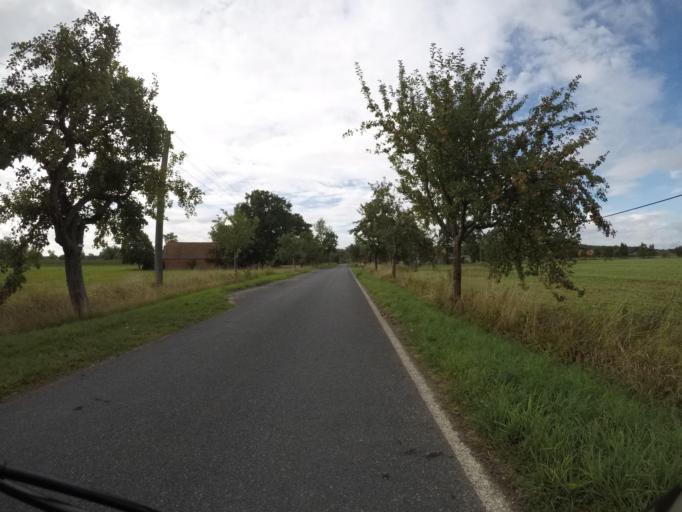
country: DE
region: Lower Saxony
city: Tosterglope
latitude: 53.2602
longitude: 10.8390
